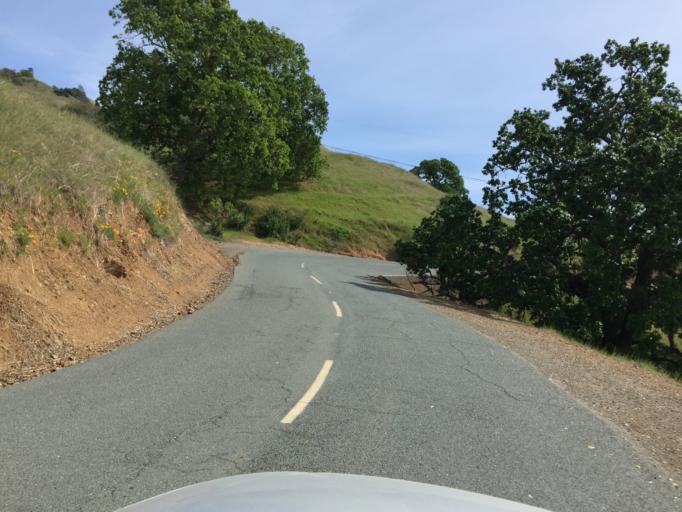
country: US
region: California
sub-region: Contra Costa County
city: Diablo
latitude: 37.8675
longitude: -121.9452
